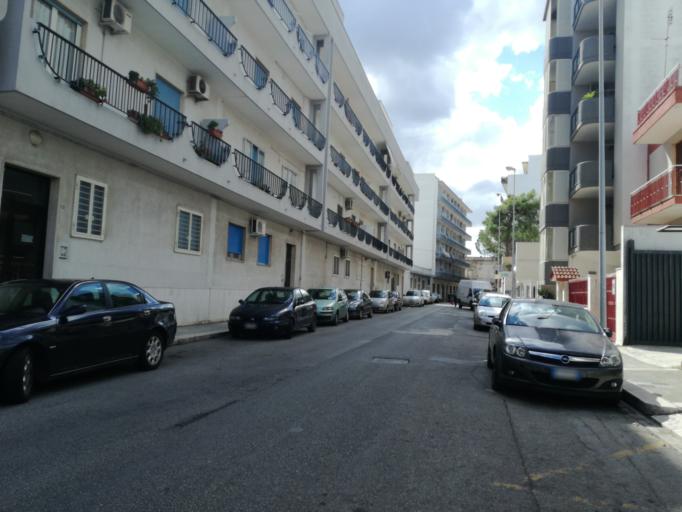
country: IT
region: Apulia
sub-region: Provincia di Bari
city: Triggiano
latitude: 41.0671
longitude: 16.9280
